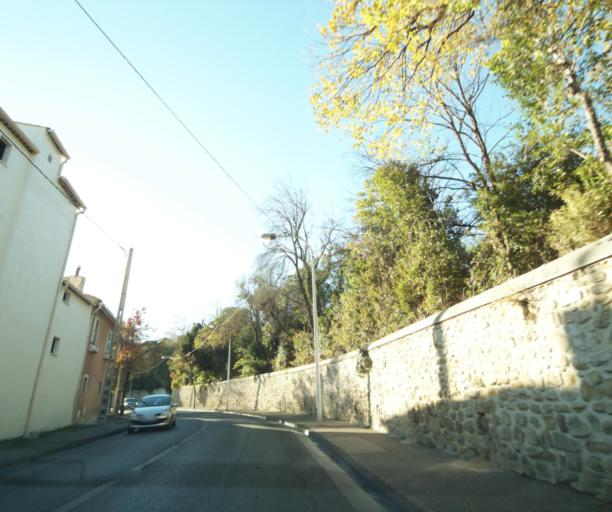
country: FR
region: Provence-Alpes-Cote d'Azur
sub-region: Departement des Bouches-du-Rhone
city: Marseille 13
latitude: 43.3251
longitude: 5.4179
